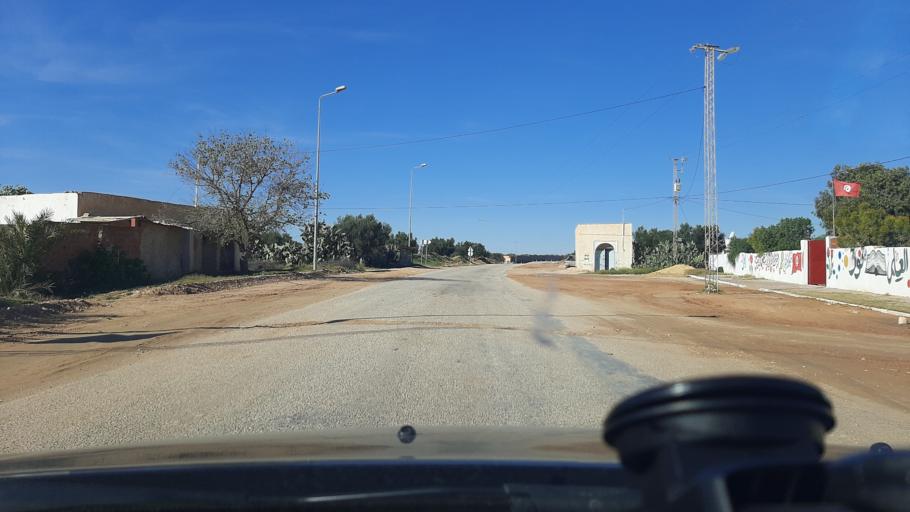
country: TN
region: Safaqis
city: Sfax
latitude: 34.9093
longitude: 10.5923
